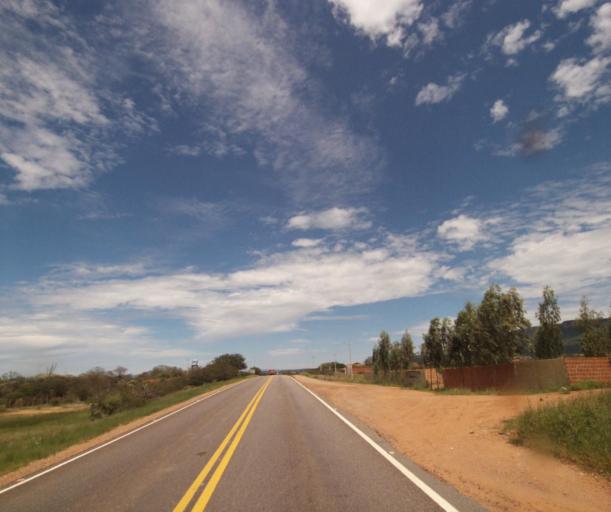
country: BR
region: Bahia
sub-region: Palmas De Monte Alto
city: Palmas de Monte Alto
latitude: -14.2506
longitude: -43.1765
